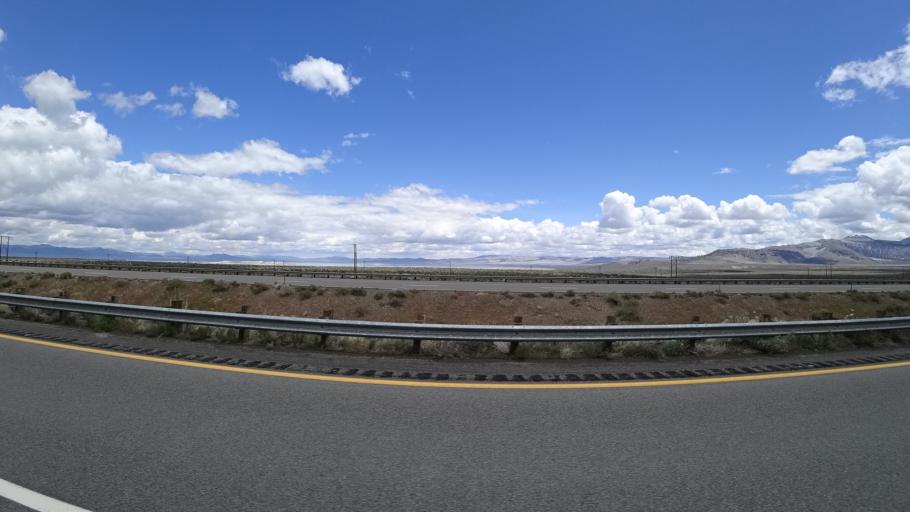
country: US
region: California
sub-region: Mono County
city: Mammoth Lakes
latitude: 37.9409
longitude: -119.1025
